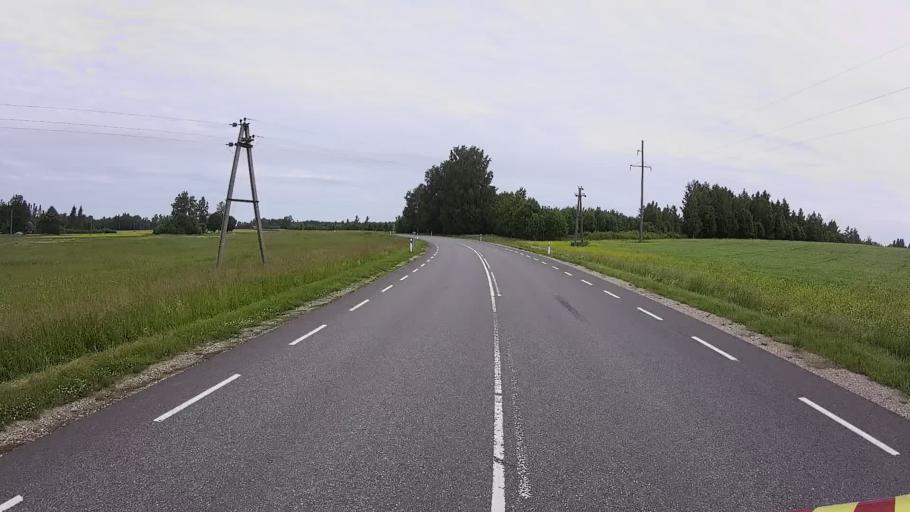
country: EE
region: Viljandimaa
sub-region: Karksi vald
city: Karksi-Nuia
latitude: 58.1519
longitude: 25.5968
